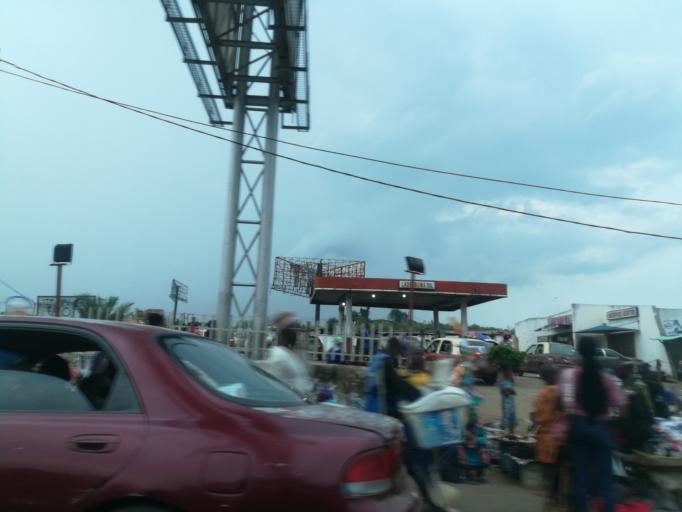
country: NG
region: Oyo
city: Moniya
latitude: 7.4679
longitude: 3.9125
